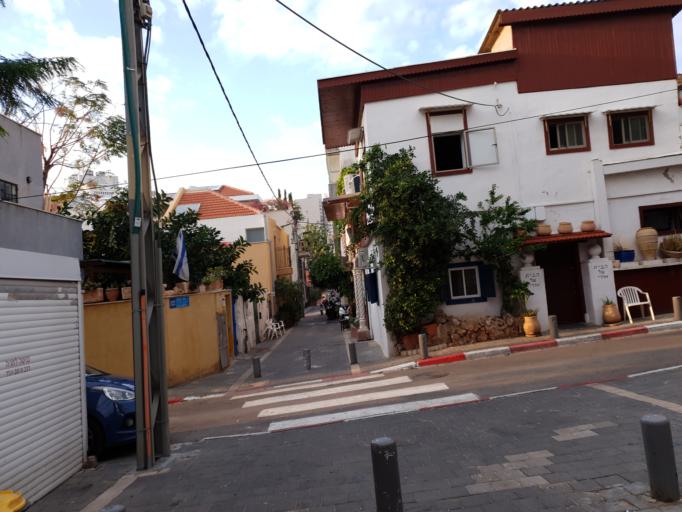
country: IL
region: Tel Aviv
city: Yafo
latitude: 32.0617
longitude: 34.7659
